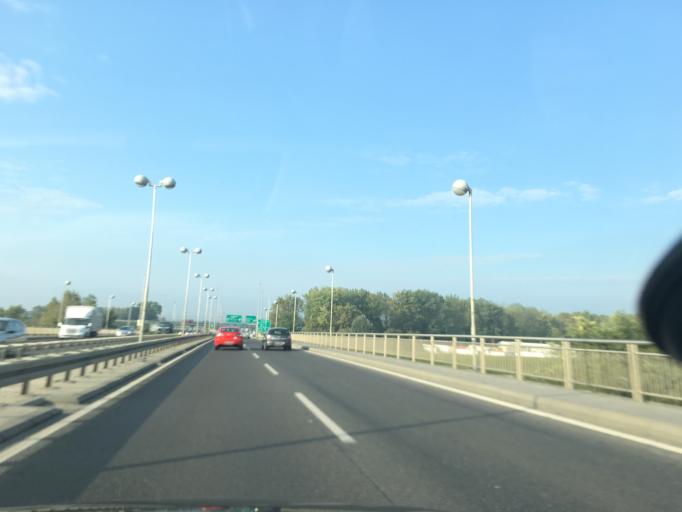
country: HR
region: Grad Zagreb
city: Jezdovec
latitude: 45.7919
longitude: 15.8538
